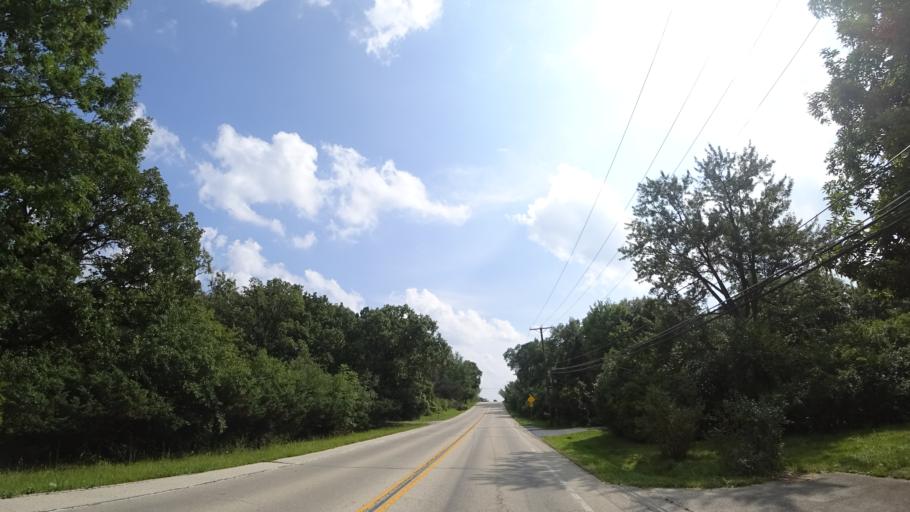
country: US
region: Illinois
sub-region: Will County
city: Goodings Grove
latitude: 41.6649
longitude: -87.8932
